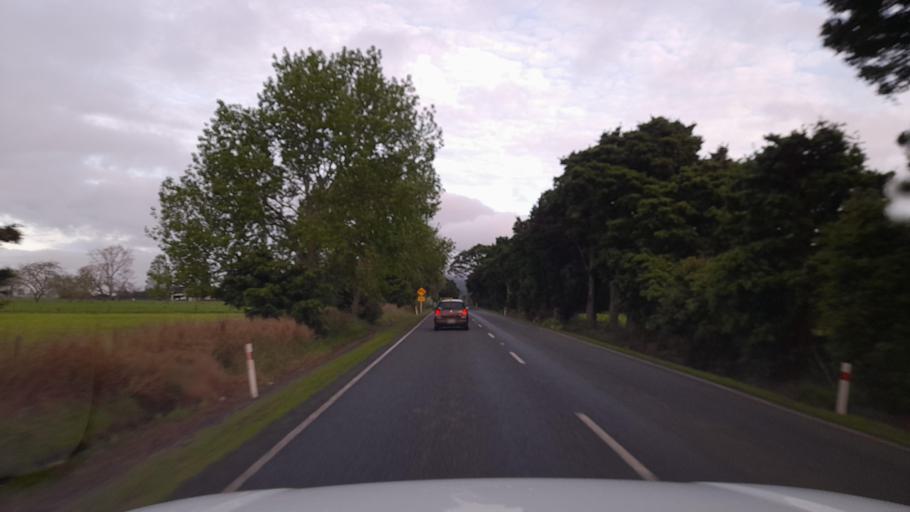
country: NZ
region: Northland
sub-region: Whangarei
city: Maungatapere
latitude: -35.7099
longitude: 173.9947
